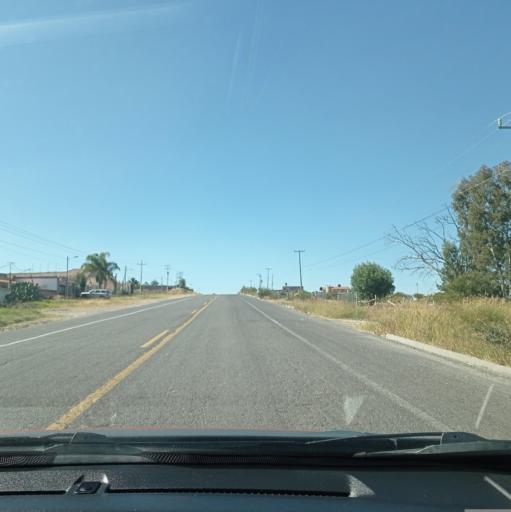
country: MX
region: Jalisco
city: San Miguel el Alto
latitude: 21.0126
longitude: -102.3144
